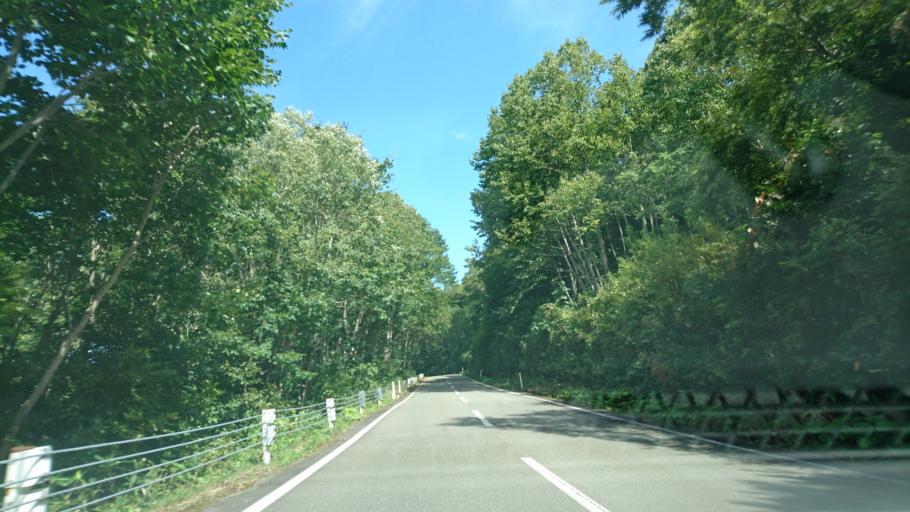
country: JP
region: Akita
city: Yuzawa
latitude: 38.9681
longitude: 140.7123
